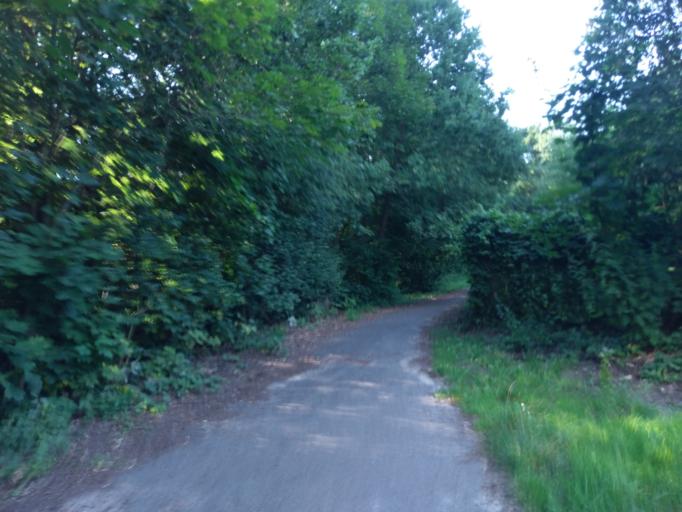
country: DE
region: Brandenburg
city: Teltow
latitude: 52.4142
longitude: 13.2486
